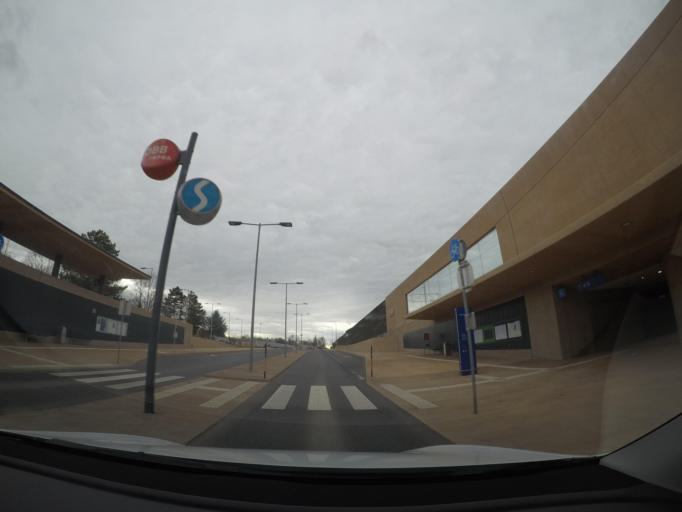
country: AT
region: Lower Austria
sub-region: Politischer Bezirk Modling
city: Achau
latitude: 48.0812
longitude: 16.3783
